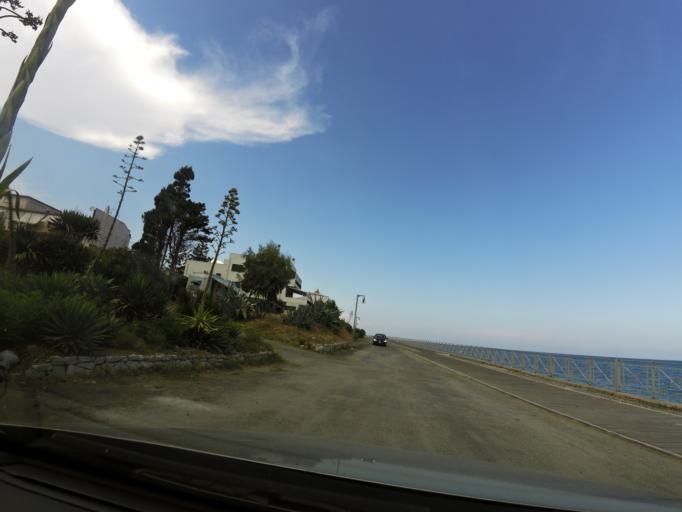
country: IT
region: Calabria
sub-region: Provincia di Reggio Calabria
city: Monasterace Marina
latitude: 38.4408
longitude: 16.5774
